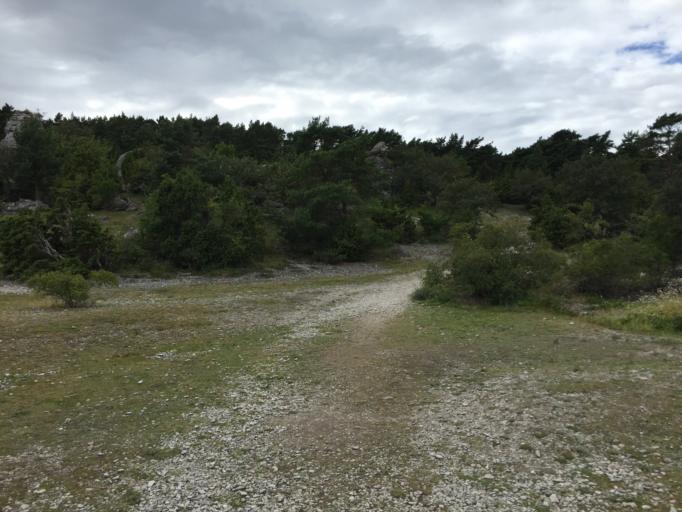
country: SE
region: Gotland
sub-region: Gotland
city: Visby
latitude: 57.8259
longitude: 18.5115
